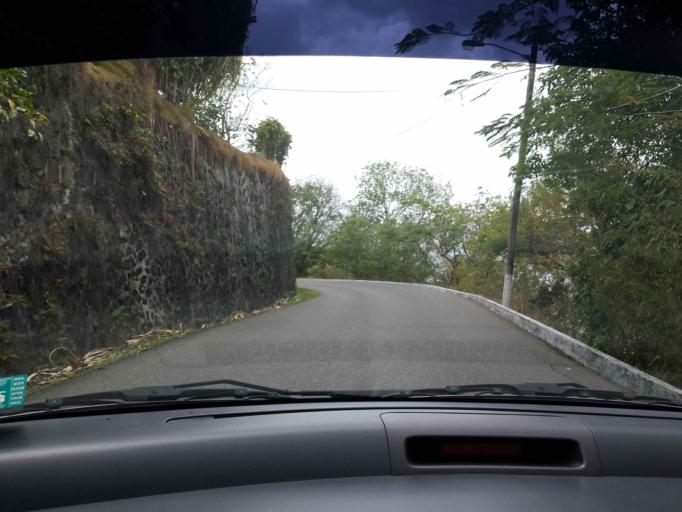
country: LC
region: Castries Quarter
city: Castries
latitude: 14.0069
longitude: -60.9980
